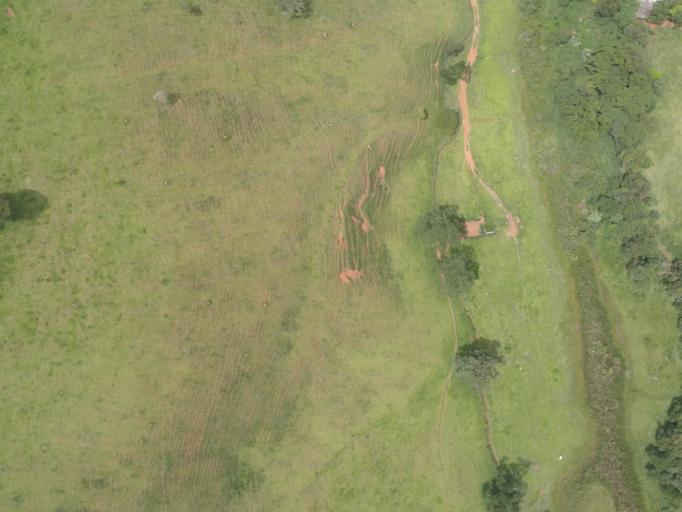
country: BR
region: Minas Gerais
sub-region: Tiradentes
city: Tiradentes
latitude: -21.0679
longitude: -44.0857
